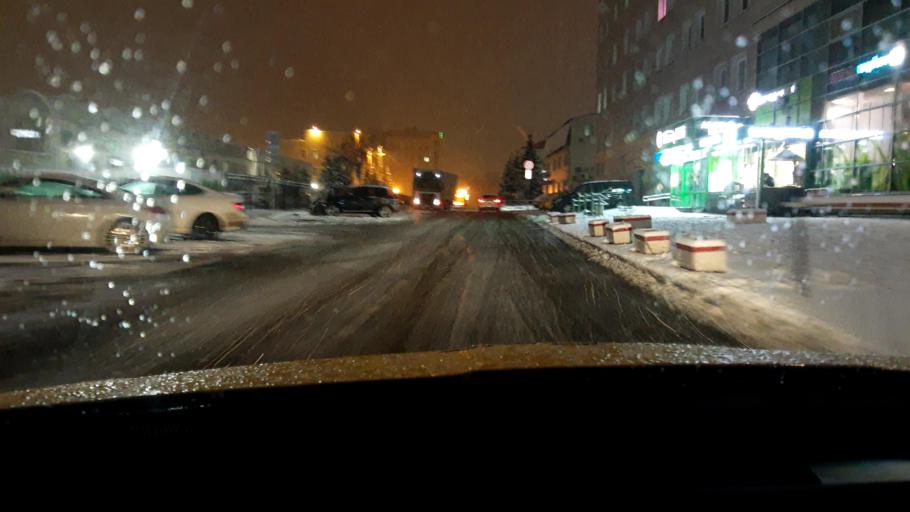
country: RU
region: Moscow
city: Kuz'minki
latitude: 55.7100
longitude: 37.8039
